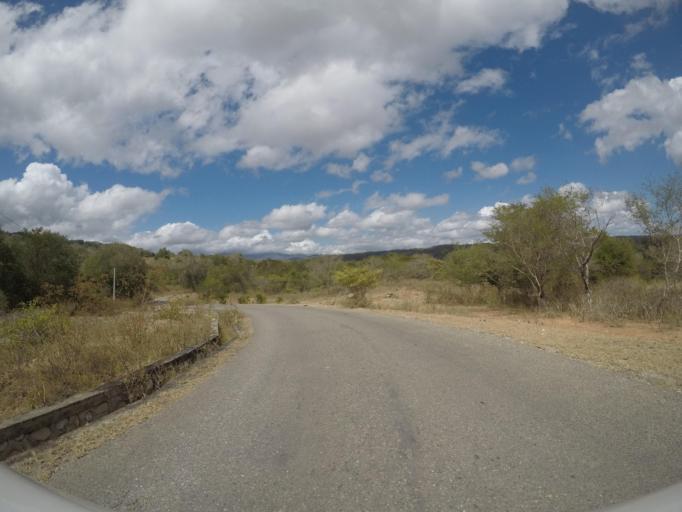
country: TL
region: Lautem
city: Lospalos
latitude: -8.4346
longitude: 126.8298
